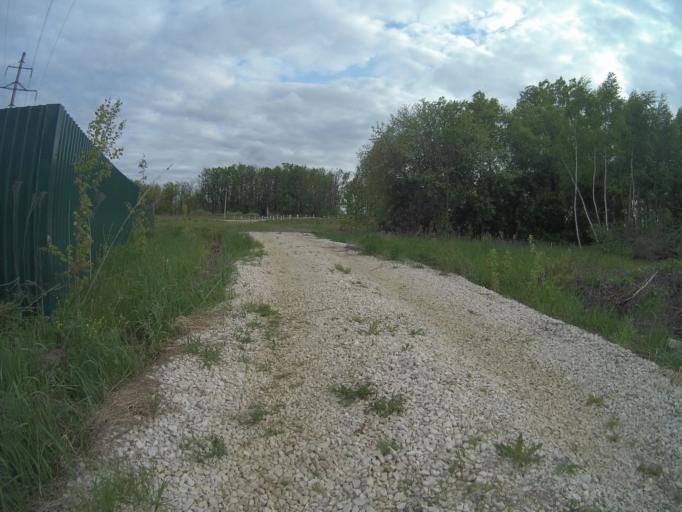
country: RU
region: Vladimir
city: Raduzhnyy
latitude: 56.0159
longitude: 40.3925
